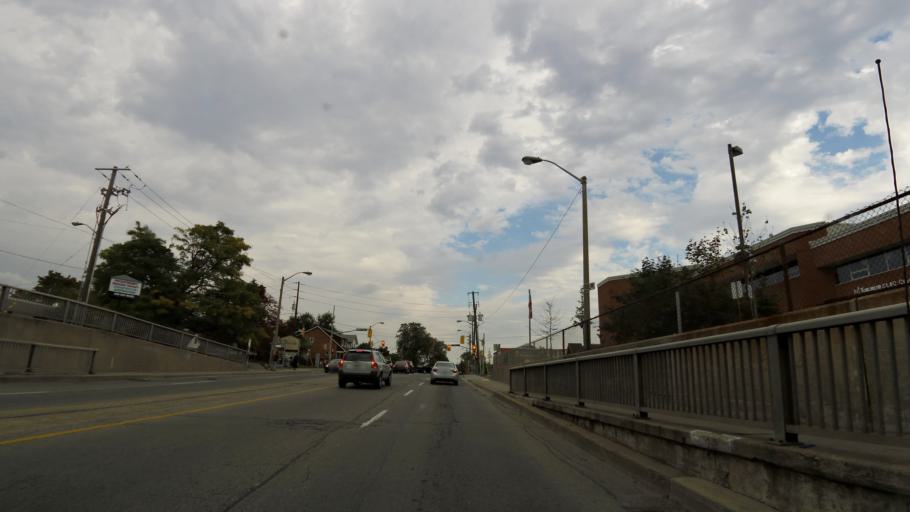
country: CA
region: Ontario
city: Etobicoke
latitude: 43.7008
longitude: -79.5130
